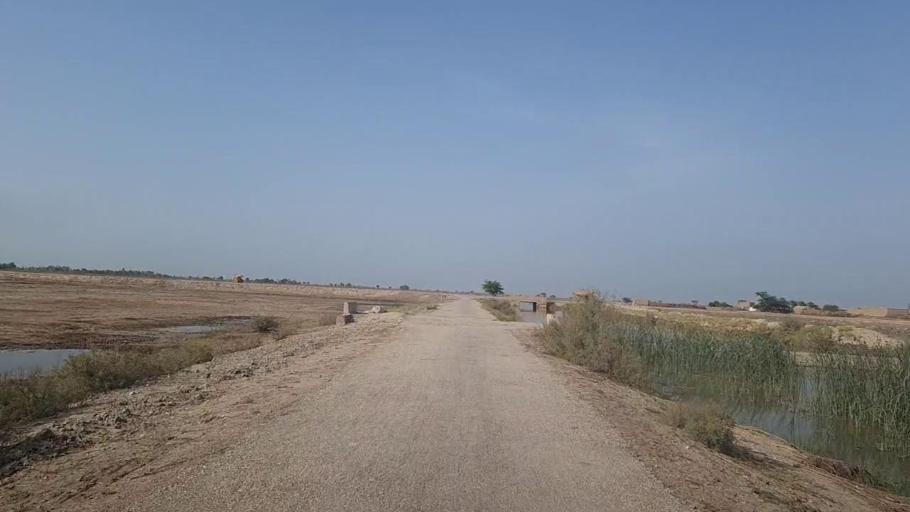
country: PK
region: Sindh
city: Mehar
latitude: 27.1161
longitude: 67.8796
